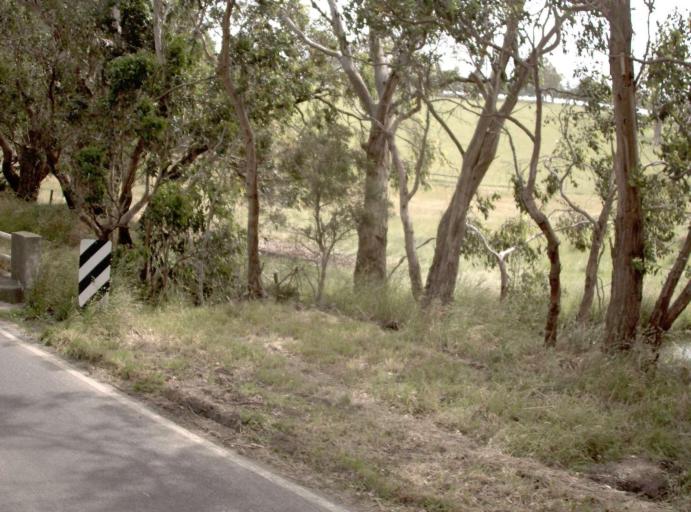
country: AU
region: Victoria
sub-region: Latrobe
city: Moe
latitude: -38.1389
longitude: 146.1467
